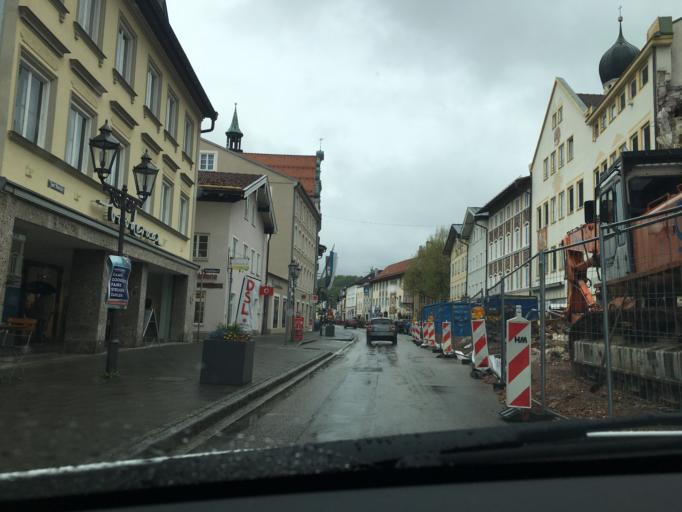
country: DE
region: Bavaria
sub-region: Upper Bavaria
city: Wolfratshausen
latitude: 47.9148
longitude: 11.4186
